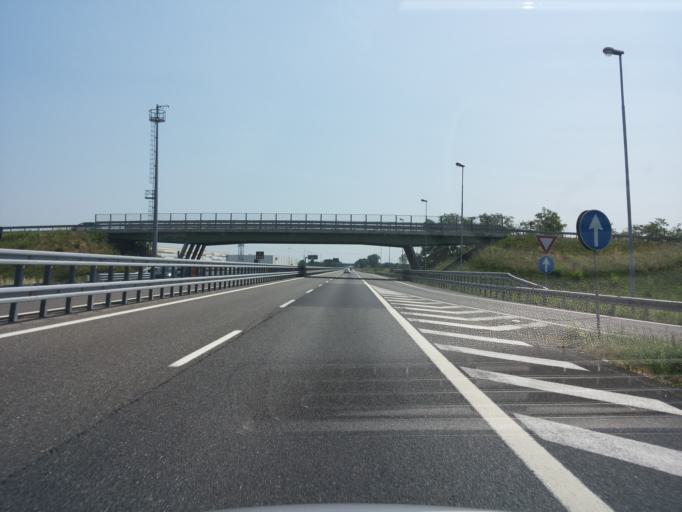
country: IT
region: Emilia-Romagna
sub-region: Provincia di Piacenza
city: Castel San Giovanni
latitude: 45.0756
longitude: 9.4505
